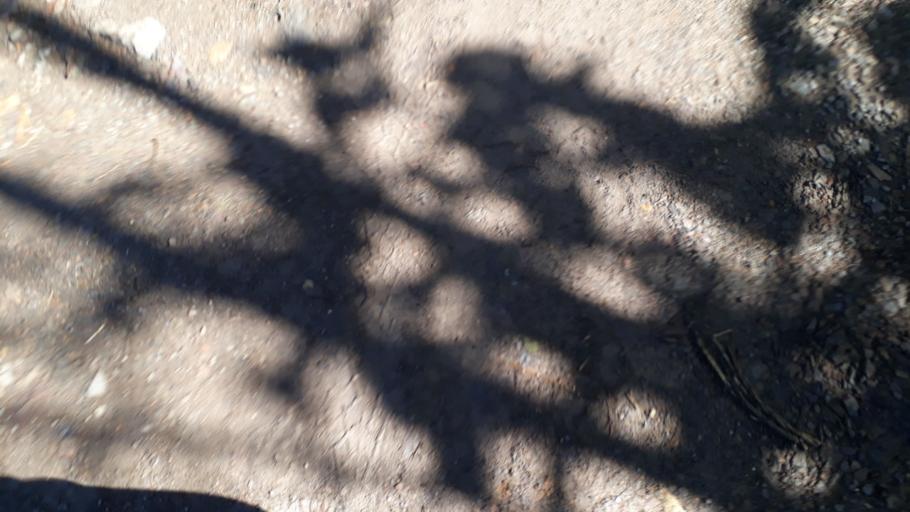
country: CO
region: Casanare
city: Nunchia
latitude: 5.6677
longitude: -72.4232
